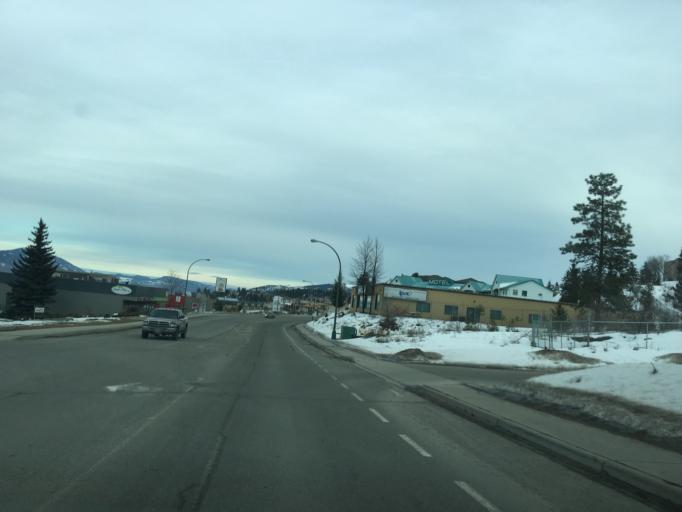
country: CA
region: British Columbia
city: Kamloops
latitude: 50.6516
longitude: -120.3789
